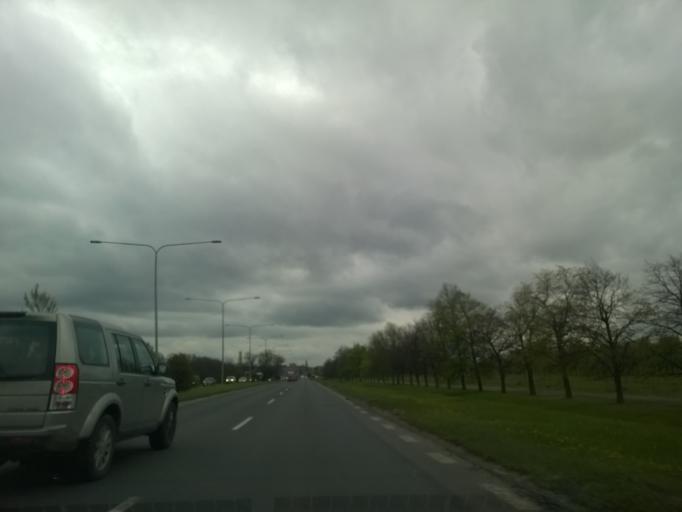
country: PL
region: Masovian Voivodeship
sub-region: Warszawa
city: Wilanow
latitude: 52.1582
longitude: 21.0878
